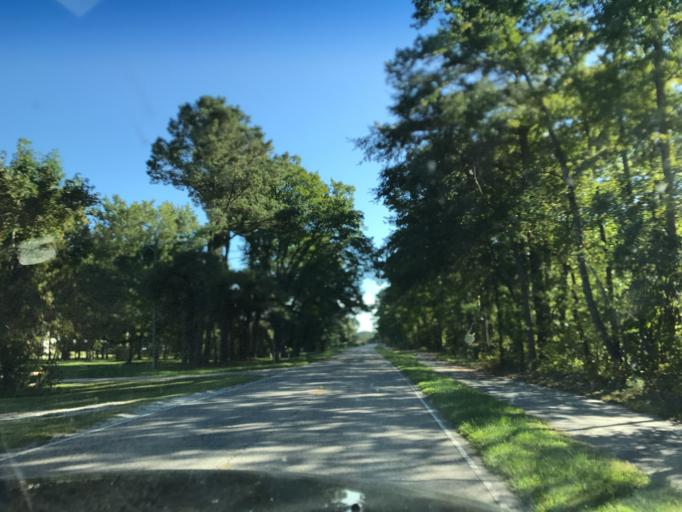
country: US
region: Virginia
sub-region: City of Portsmouth
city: Portsmouth Heights
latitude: 36.7004
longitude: -76.3562
